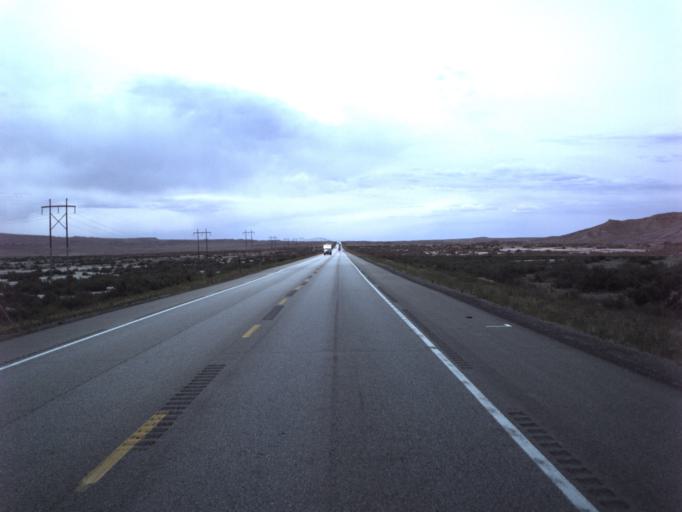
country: US
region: Utah
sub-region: Carbon County
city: East Carbon City
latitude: 39.2479
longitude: -110.3389
